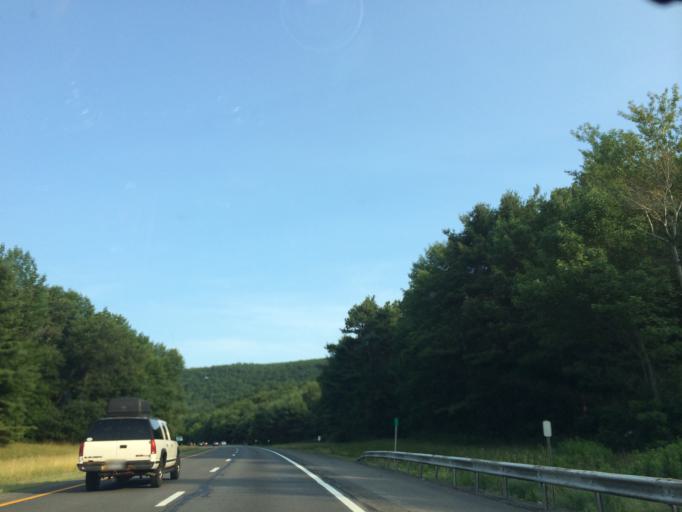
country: US
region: Massachusetts
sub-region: Berkshire County
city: Richmond
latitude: 42.3712
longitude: -73.4600
